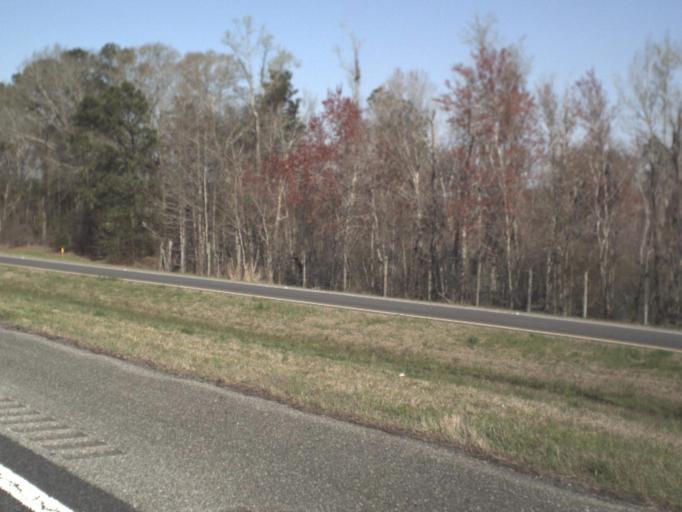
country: US
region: Florida
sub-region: Gadsden County
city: Gretna
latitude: 30.5791
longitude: -84.7024
